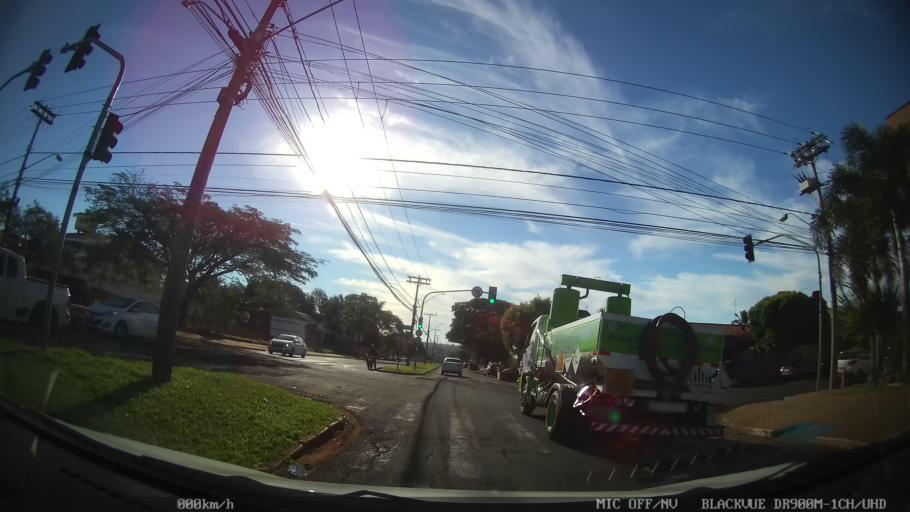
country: BR
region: Sao Paulo
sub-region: Araraquara
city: Araraquara
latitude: -21.7678
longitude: -48.1719
